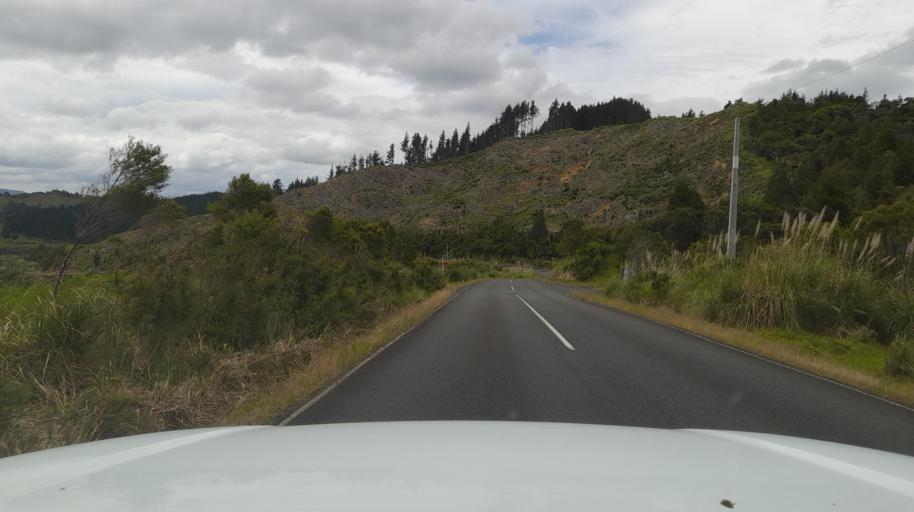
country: NZ
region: Northland
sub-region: Far North District
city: Kaitaia
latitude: -35.3722
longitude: 173.4301
